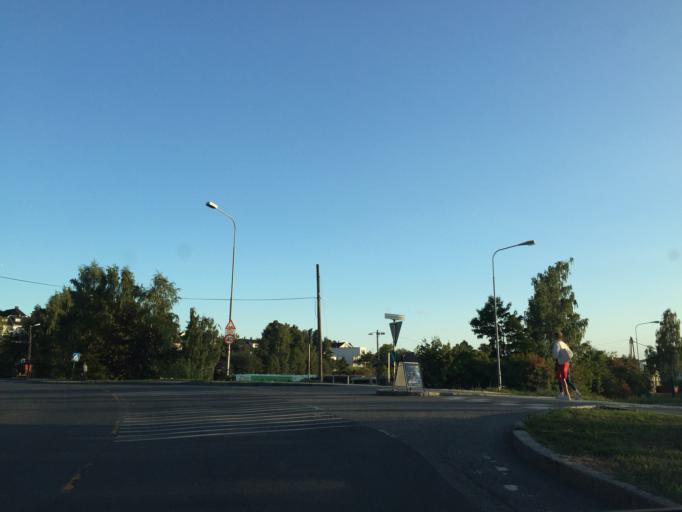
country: NO
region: Akershus
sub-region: Baerum
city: Lysaker
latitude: 59.8884
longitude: 10.6210
